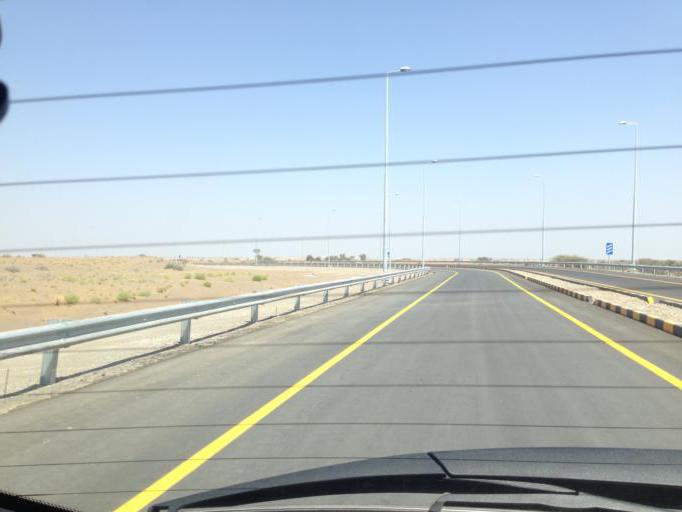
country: OM
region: Al Batinah
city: Rustaq
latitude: 23.5372
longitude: 57.5657
